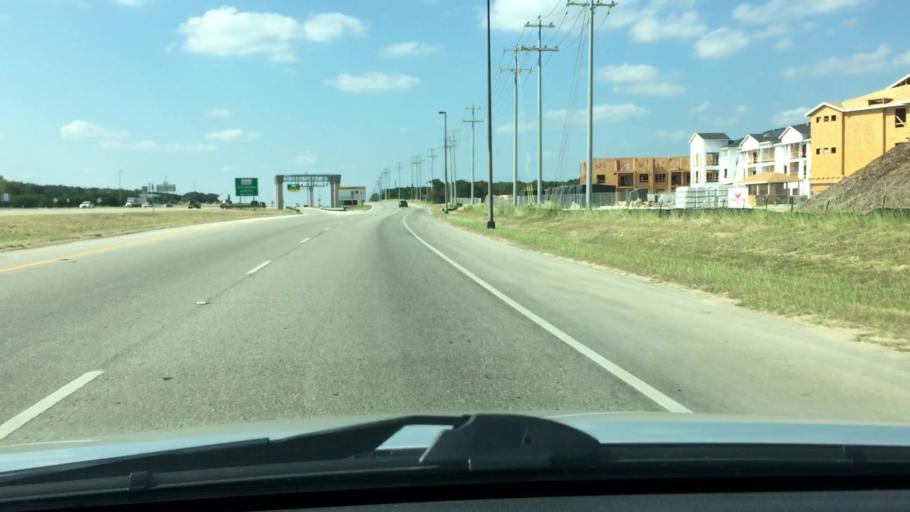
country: US
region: Texas
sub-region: Williamson County
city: Leander
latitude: 30.5668
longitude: -97.8263
